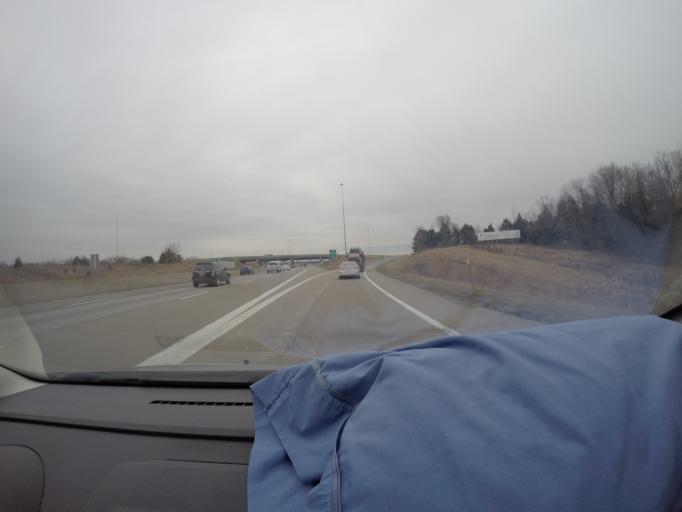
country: US
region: Missouri
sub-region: Saint Charles County
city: Wentzville
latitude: 38.8061
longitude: -90.8417
